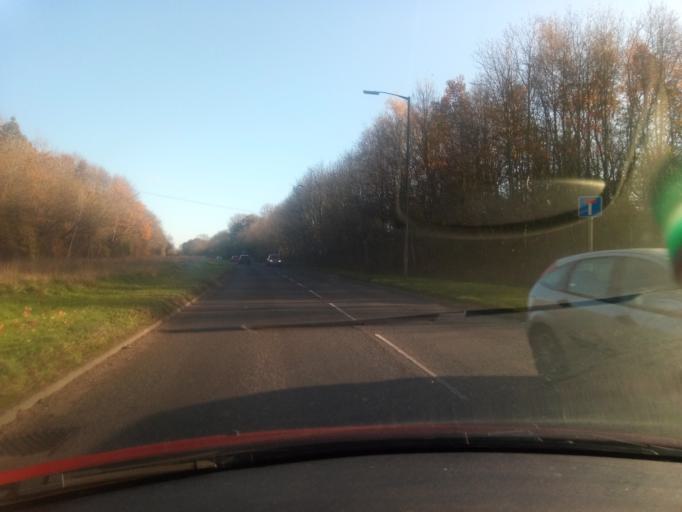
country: GB
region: England
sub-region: Derbyshire
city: Heage
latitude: 53.0609
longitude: -1.4379
